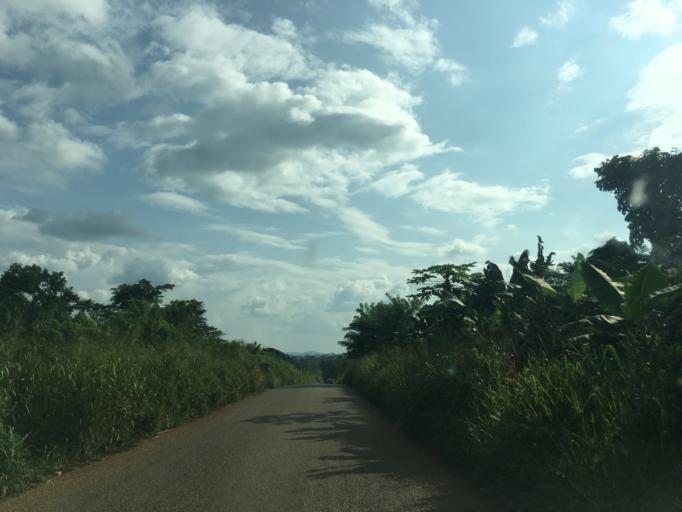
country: GH
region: Western
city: Bibiani
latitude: 6.7707
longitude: -2.5686
